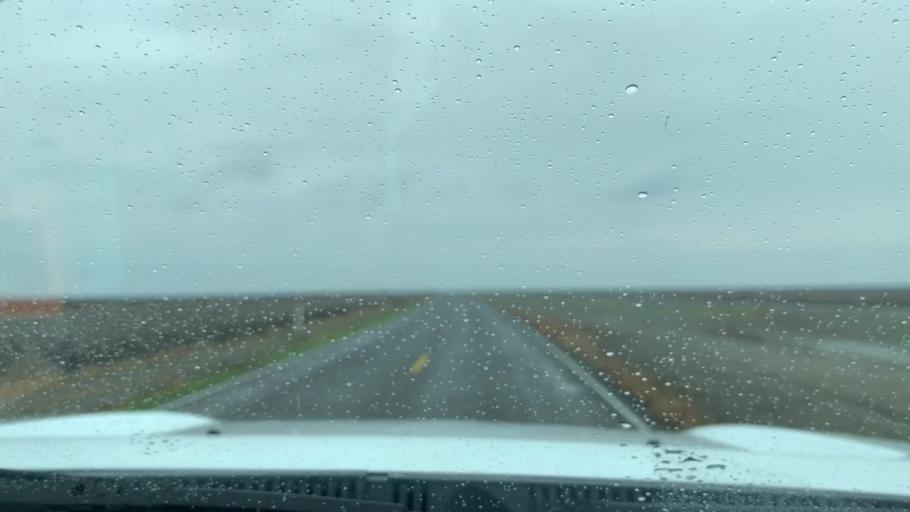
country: US
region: California
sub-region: Tulare County
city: Alpaugh
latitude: 35.9339
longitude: -119.6649
